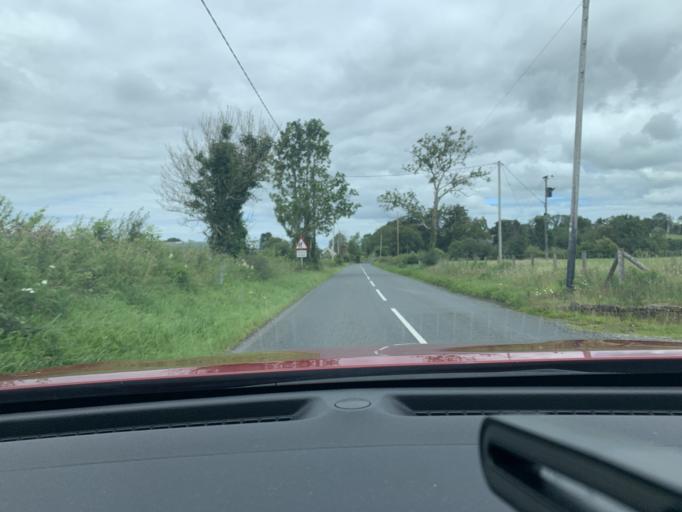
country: GB
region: Northern Ireland
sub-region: Fermanagh District
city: Enniskillen
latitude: 54.2791
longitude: -7.7024
